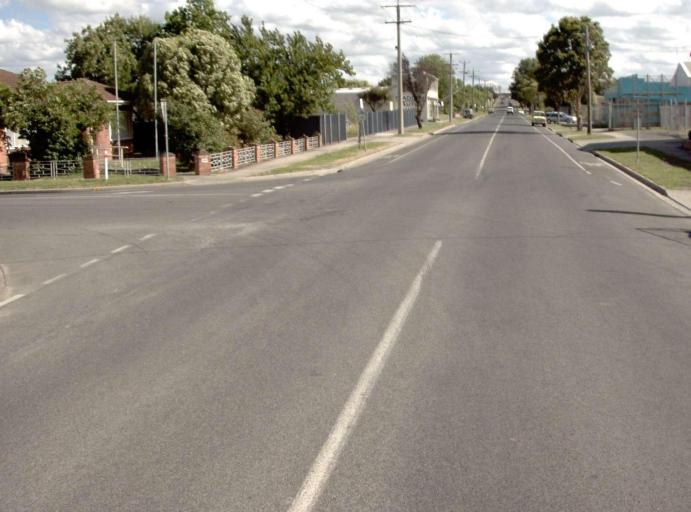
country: AU
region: Victoria
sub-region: Latrobe
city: Morwell
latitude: -38.2285
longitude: 146.3960
